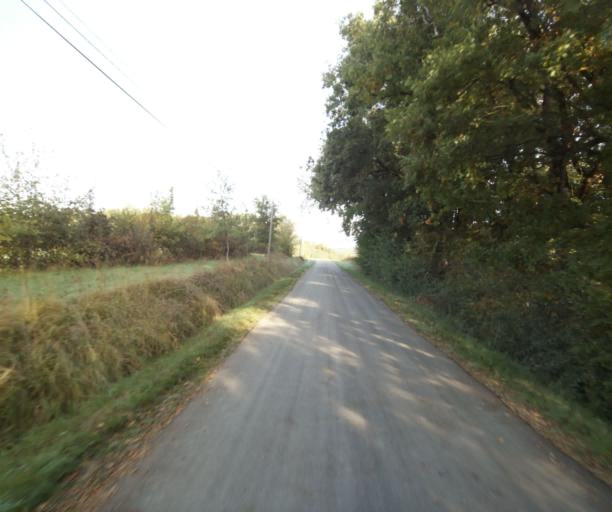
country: FR
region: Midi-Pyrenees
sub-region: Departement de la Haute-Garonne
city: Villemur-sur-Tarn
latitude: 43.9186
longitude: 1.5082
